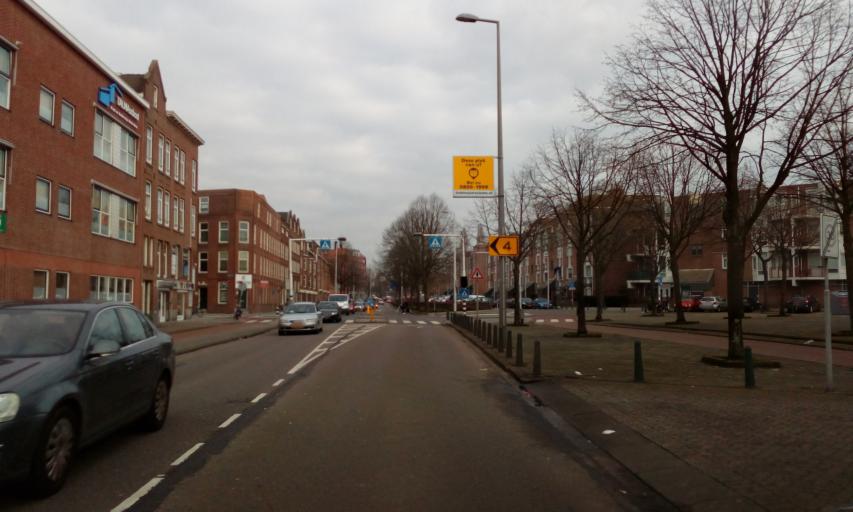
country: NL
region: South Holland
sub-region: Gemeente Rotterdam
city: Rotterdam
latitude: 51.9335
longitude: 4.4979
